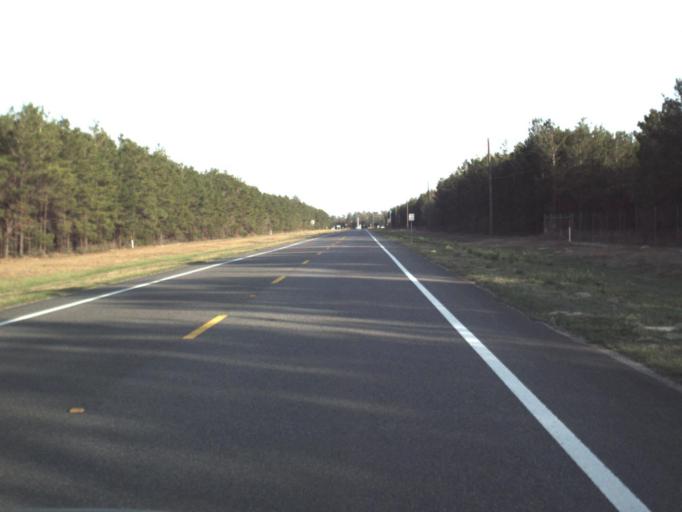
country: US
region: Florida
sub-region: Bay County
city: Lynn Haven
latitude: 30.4353
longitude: -85.6961
